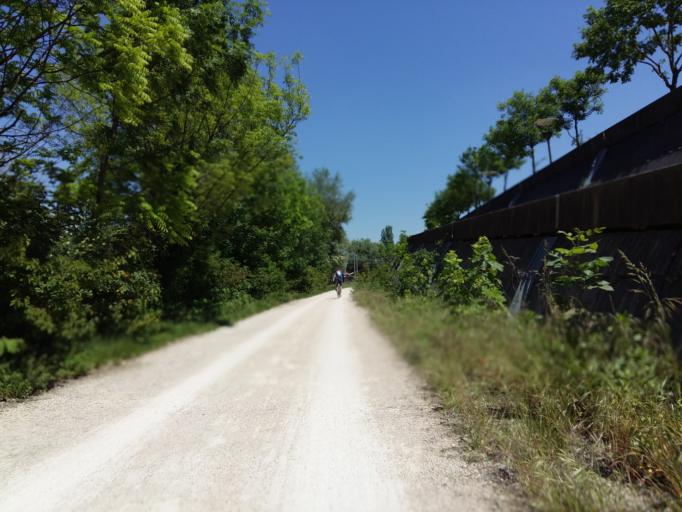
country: FR
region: Rhone-Alpes
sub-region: Departement du Rhone
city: Caluire-et-Cuire
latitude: 45.7858
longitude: 4.8530
